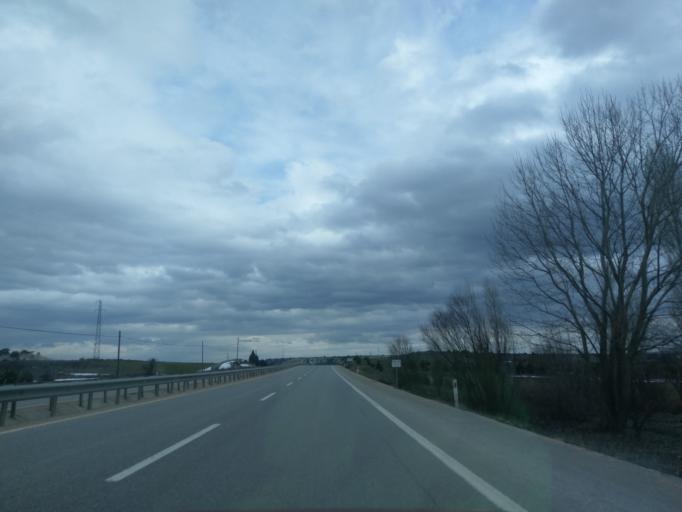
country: TR
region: Eskisehir
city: Eskisehir
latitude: 39.7251
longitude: 30.3299
